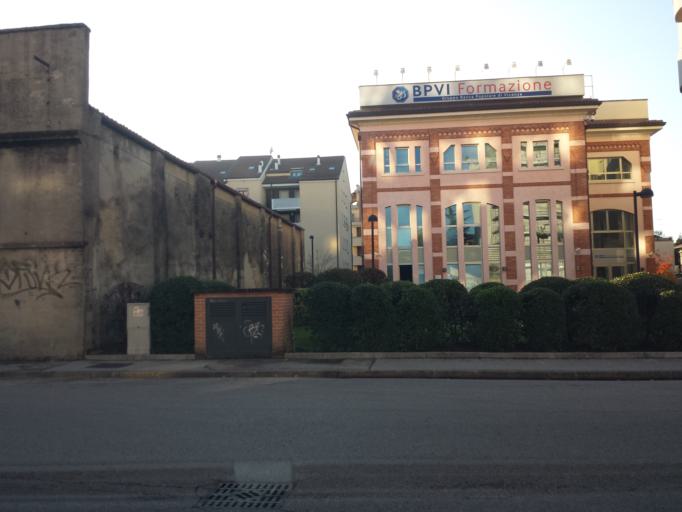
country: IT
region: Veneto
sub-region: Provincia di Vicenza
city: Vicenza
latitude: 45.5497
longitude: 11.5318
